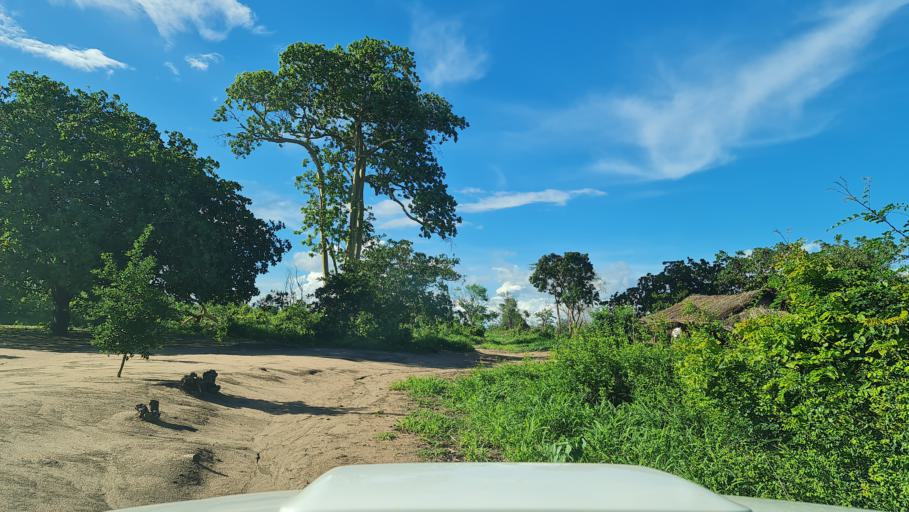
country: MZ
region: Nampula
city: Ilha de Mocambique
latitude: -15.2681
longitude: 40.1867
